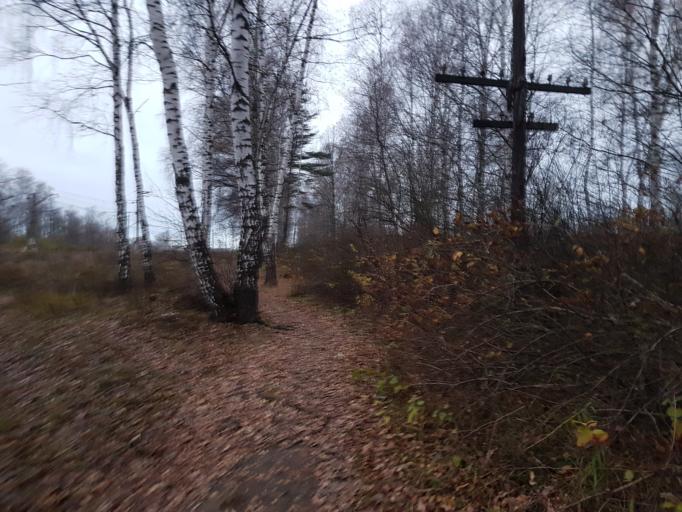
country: RU
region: Moskovskaya
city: Istra
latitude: 55.9023
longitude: 36.8712
